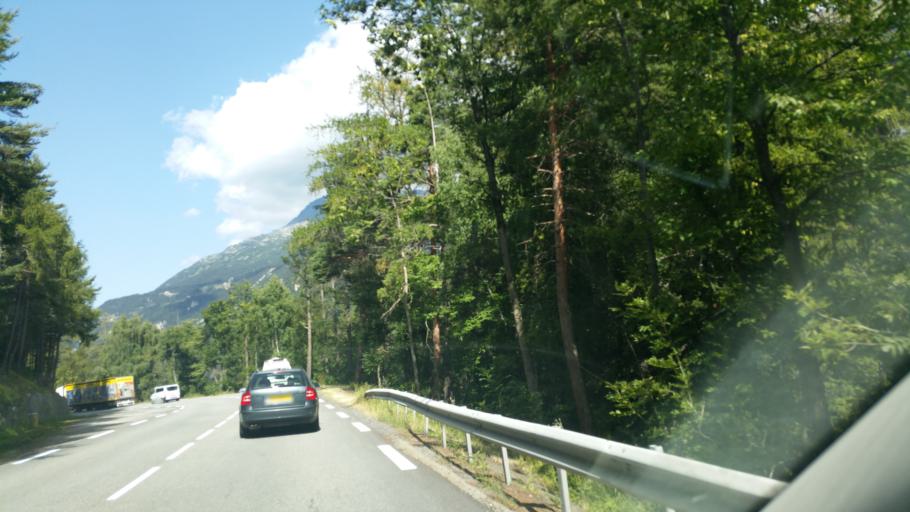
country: FR
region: Rhone-Alpes
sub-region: Departement de la Savoie
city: Modane
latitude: 45.2074
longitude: 6.7150
